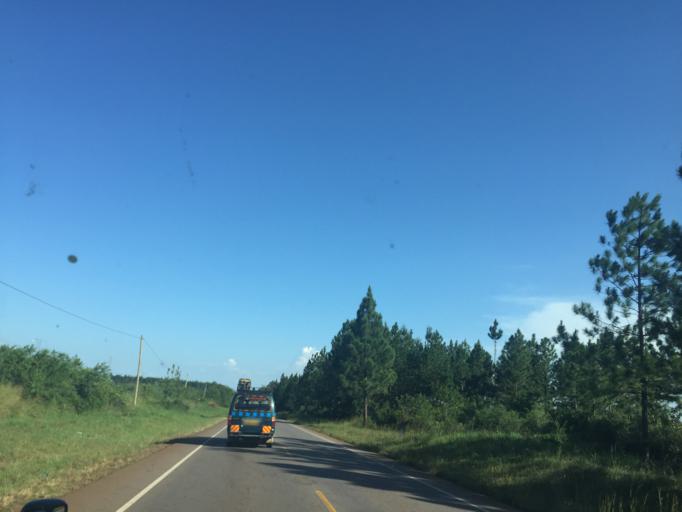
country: UG
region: Central Region
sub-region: Nakasongola District
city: Nakasongola
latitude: 1.3818
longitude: 32.3370
